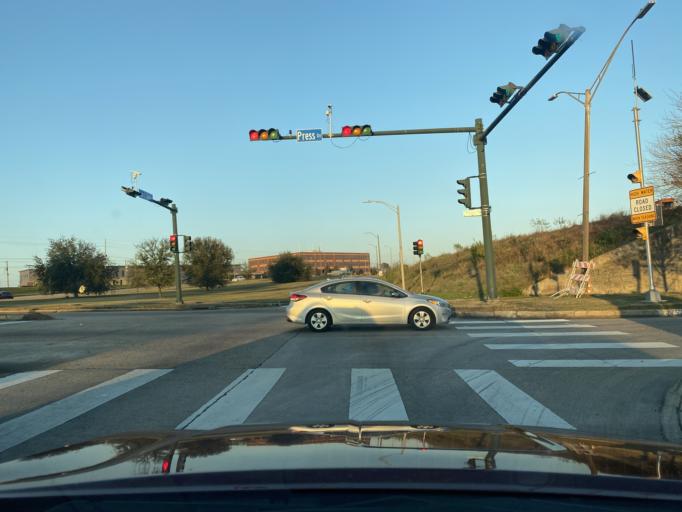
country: US
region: Louisiana
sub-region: Orleans Parish
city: New Orleans
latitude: 30.0284
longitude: -90.0455
